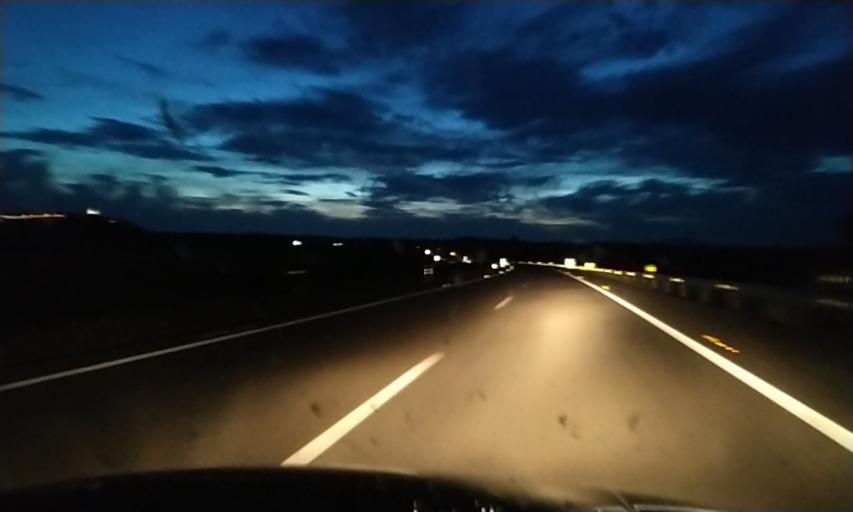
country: ES
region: Extremadura
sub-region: Provincia de Caceres
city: Galisteo
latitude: 39.9814
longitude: -6.2474
